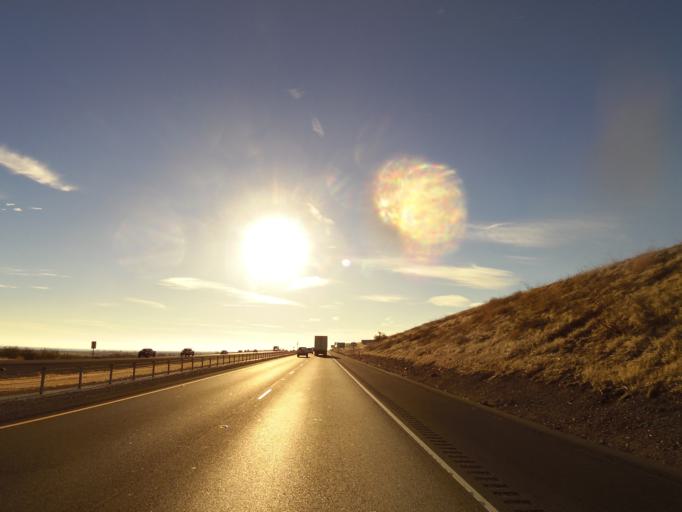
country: US
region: California
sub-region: Stanislaus County
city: Patterson
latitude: 37.5507
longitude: -121.2817
